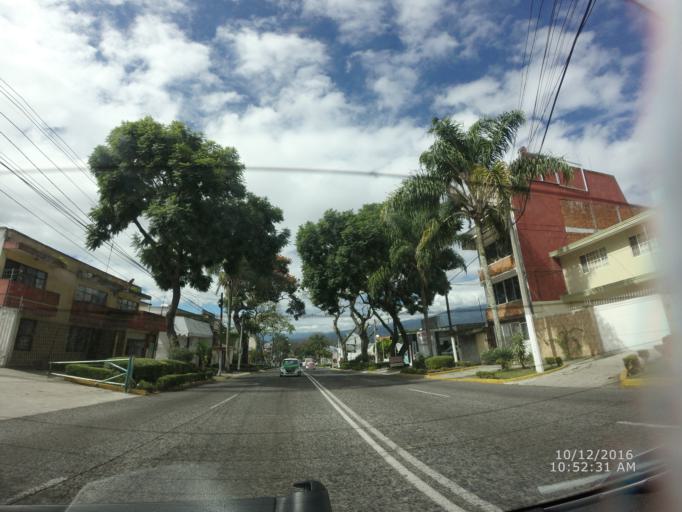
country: MX
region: Veracruz
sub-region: Xalapa
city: Xalapa de Enriquez
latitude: 19.5380
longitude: -96.9290
